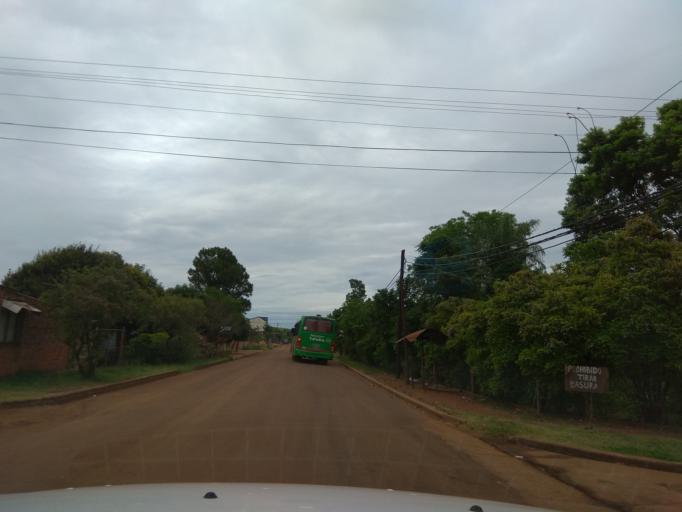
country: AR
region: Misiones
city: Garupa
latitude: -27.4408
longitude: -55.8591
